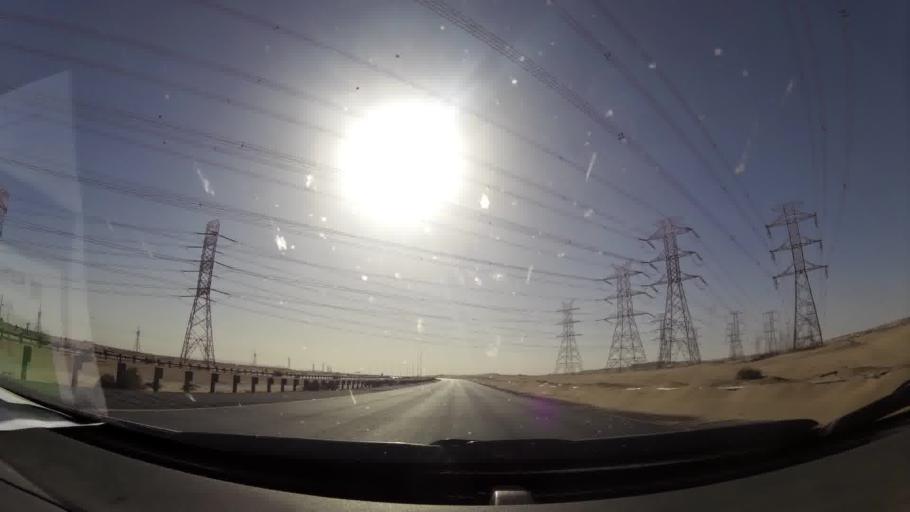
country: KW
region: Al Asimah
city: Kuwait City
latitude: 29.6266
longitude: 47.9242
